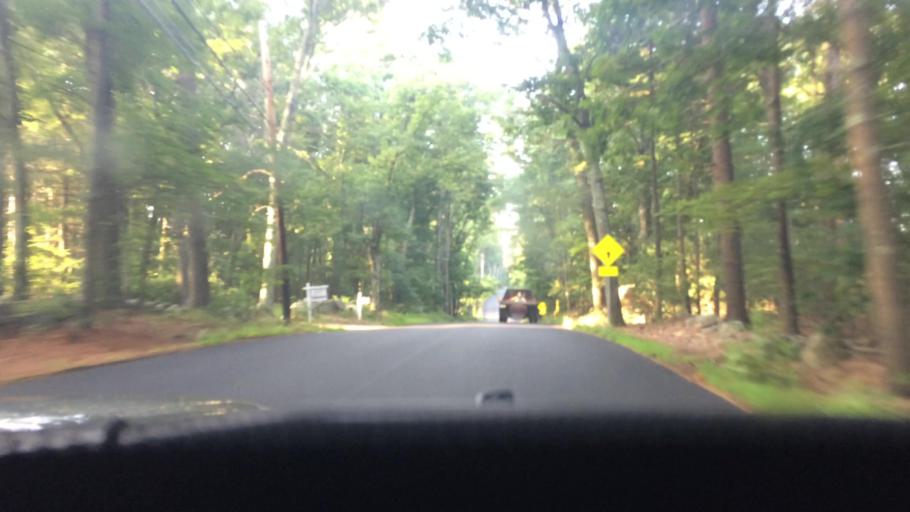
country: US
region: Massachusetts
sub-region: Middlesex County
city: North Reading
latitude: 42.6195
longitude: -71.0938
